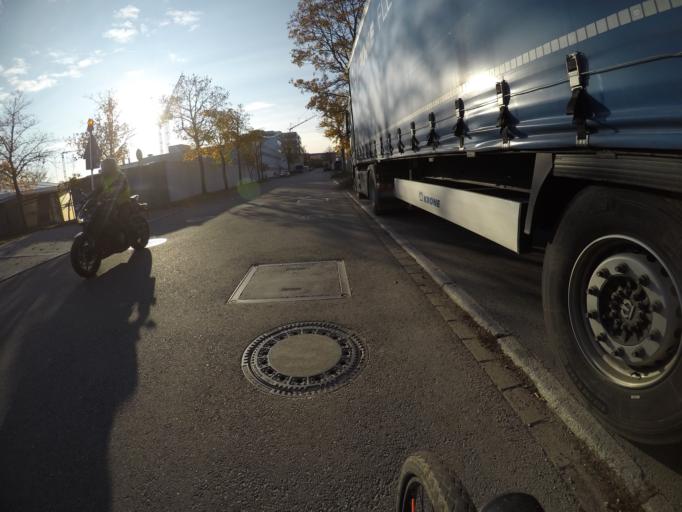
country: DE
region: Baden-Wuerttemberg
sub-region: Regierungsbezirk Stuttgart
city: Leinfelden-Echterdingen
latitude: 48.6953
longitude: 9.1482
